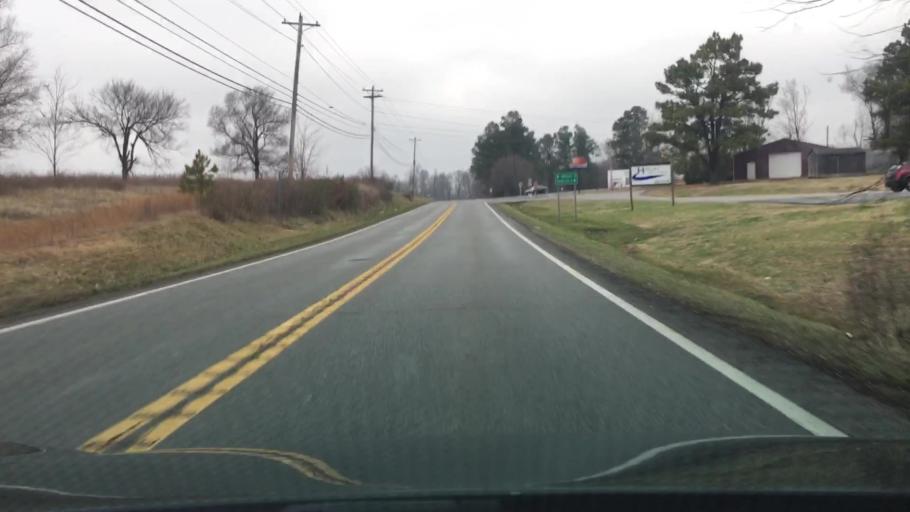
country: US
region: Kentucky
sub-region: Marshall County
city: Calvert City
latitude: 36.9458
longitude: -88.3648
